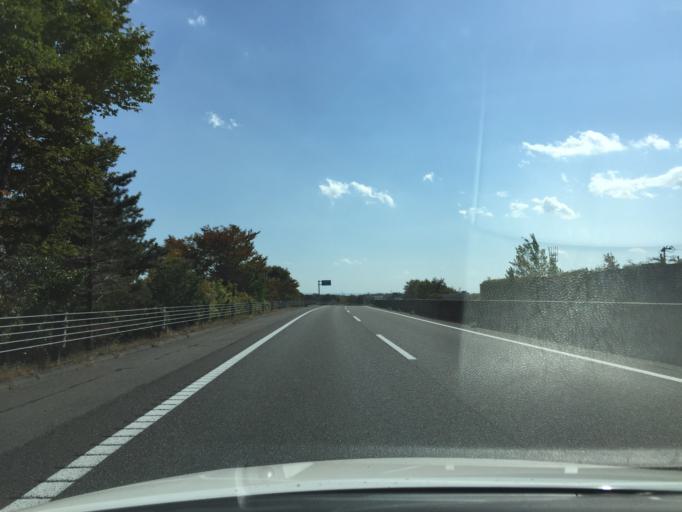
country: JP
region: Fukushima
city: Sukagawa
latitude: 37.3044
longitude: 140.3486
